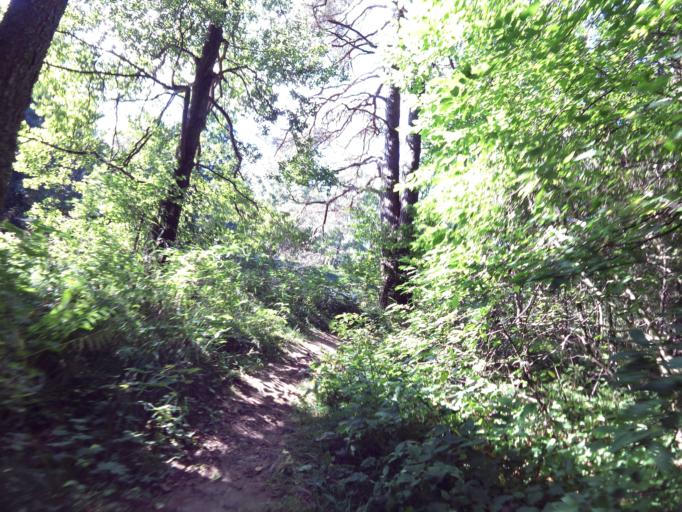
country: SE
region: Gaevleborg
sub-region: Gavle Kommun
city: Gavle
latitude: 60.7085
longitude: 17.1543
